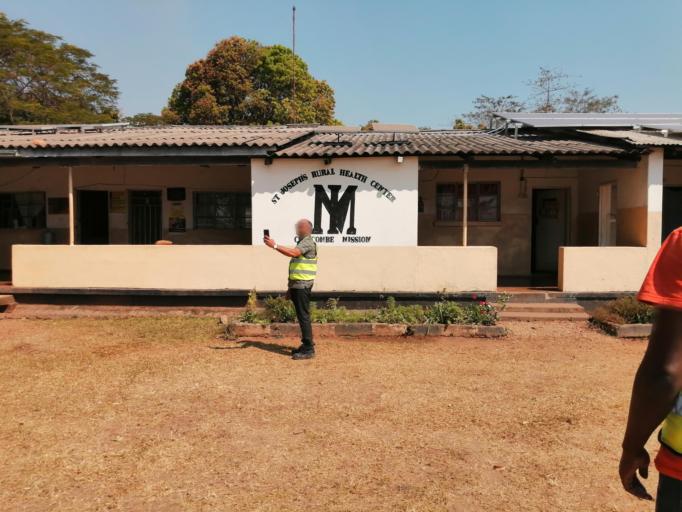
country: ZM
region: Eastern
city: Nyimba
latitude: -14.4194
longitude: 29.9705
